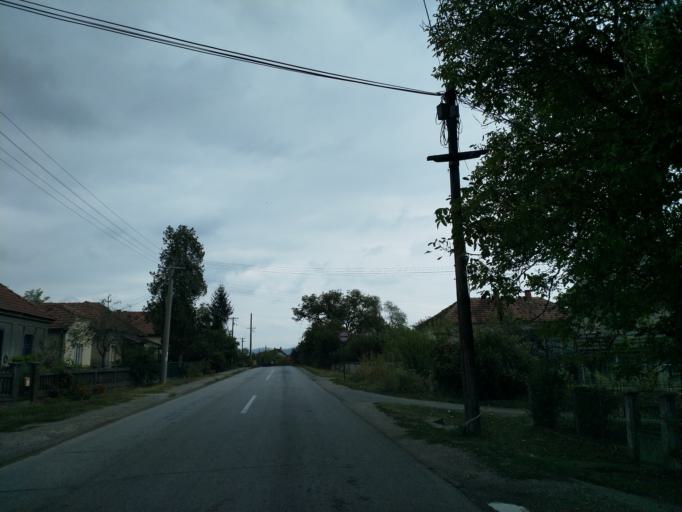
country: RS
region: Central Serbia
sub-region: Sumadijski Okrug
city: Batocina
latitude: 44.0771
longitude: 21.1806
